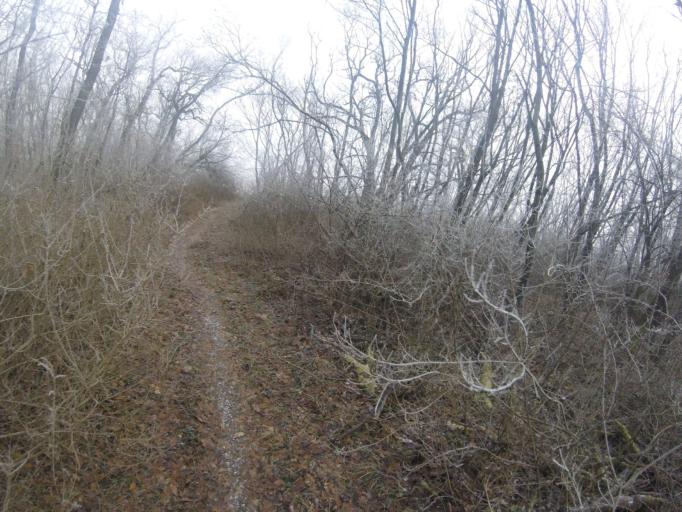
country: HU
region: Fejer
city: Csakvar
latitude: 47.3905
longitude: 18.4067
